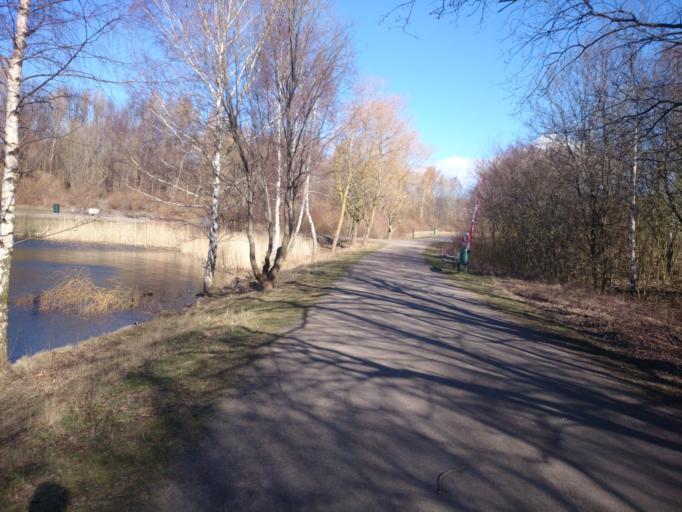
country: SE
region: Skane
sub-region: Burlovs Kommun
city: Arloev
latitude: 55.6012
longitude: 13.0702
